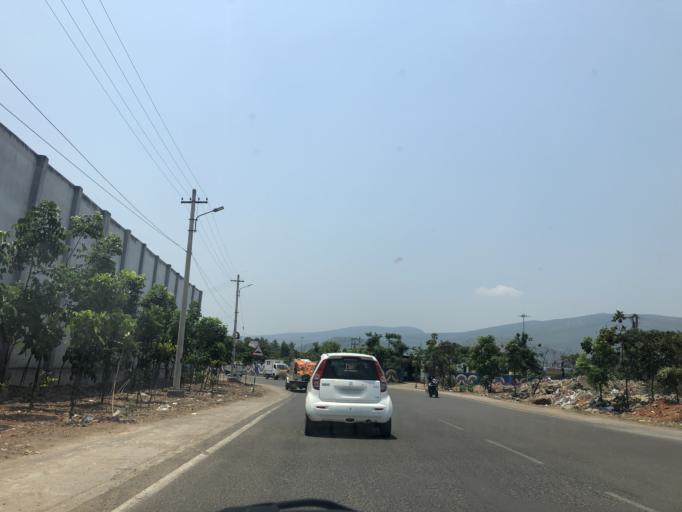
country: IN
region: Andhra Pradesh
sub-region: Vishakhapatnam
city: Yarada
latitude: 17.7163
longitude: 83.2915
